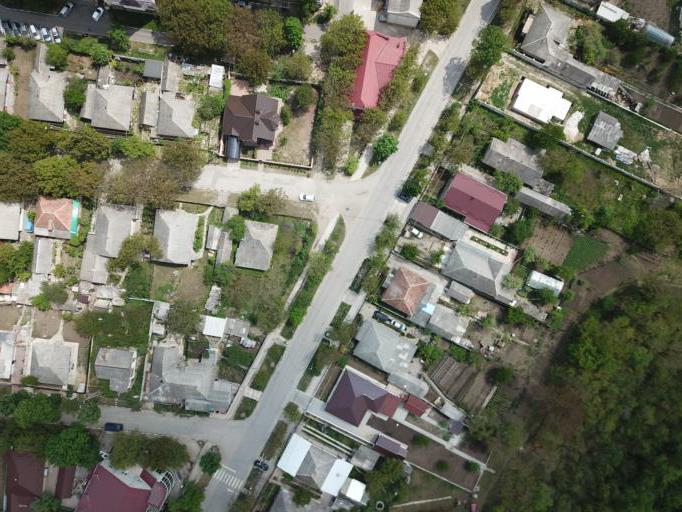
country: MD
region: Ungheni
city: Ungheni
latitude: 47.2084
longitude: 27.7937
